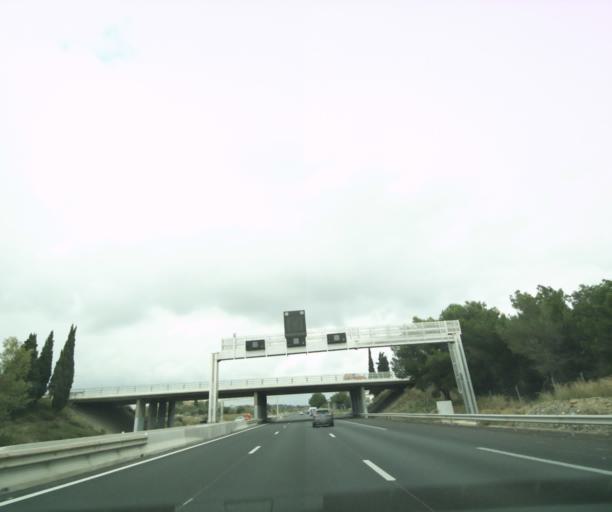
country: FR
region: Languedoc-Roussillon
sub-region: Departement de l'Herault
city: Meze
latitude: 43.4416
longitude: 3.5717
